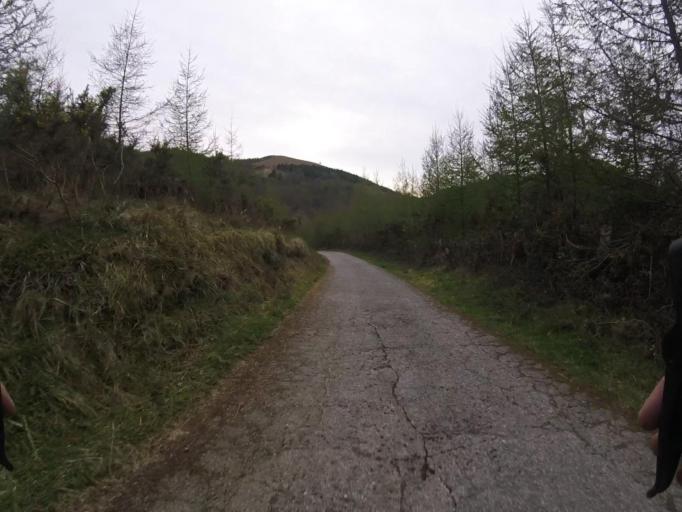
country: ES
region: Navarre
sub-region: Provincia de Navarra
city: Lesaka
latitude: 43.2725
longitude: -1.7516
